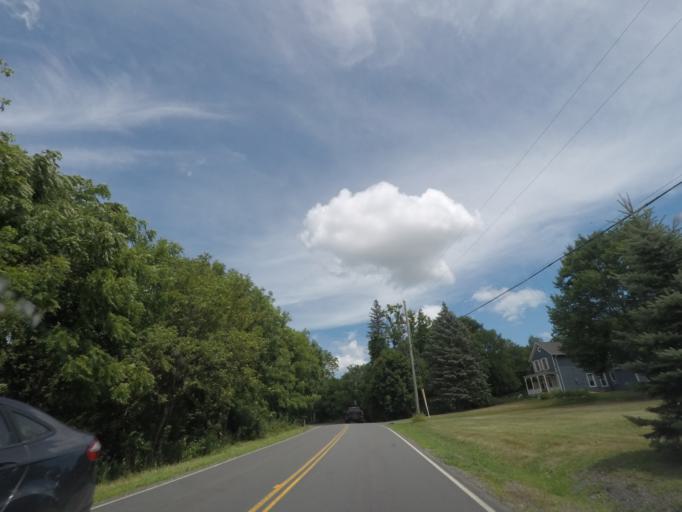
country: US
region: New York
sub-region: Rensselaer County
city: Wynantskill
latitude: 42.7005
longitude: -73.6191
